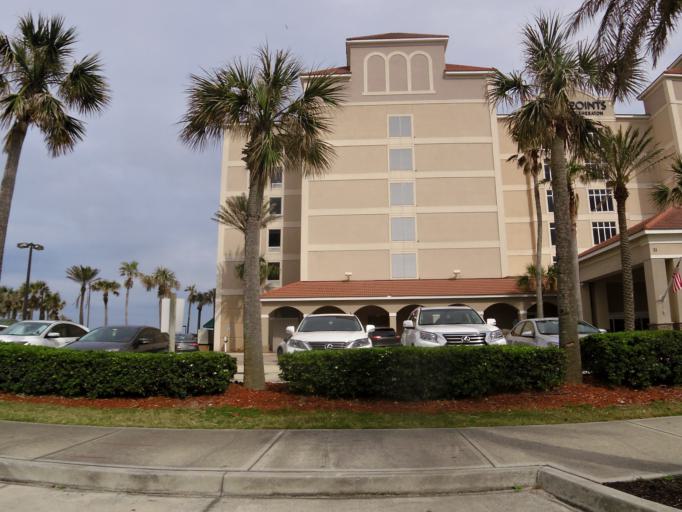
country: US
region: Florida
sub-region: Duval County
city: Jacksonville Beach
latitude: 30.2894
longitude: -81.3896
